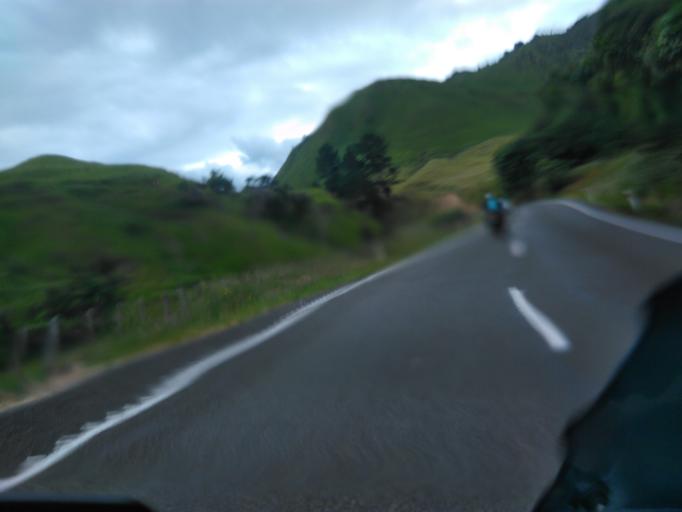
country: NZ
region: Bay of Plenty
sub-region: Opotiki District
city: Opotiki
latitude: -38.3718
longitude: 177.4651
